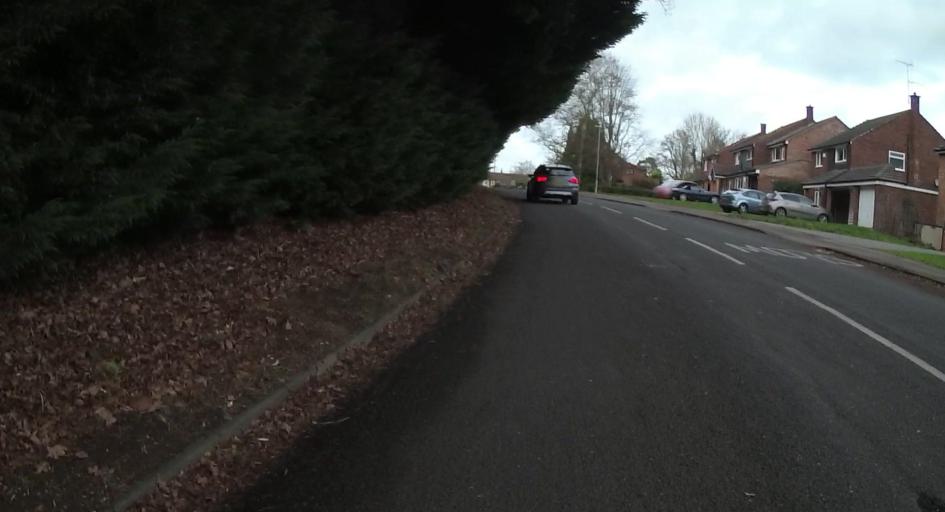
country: GB
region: England
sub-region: Wokingham
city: Wokingham
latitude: 51.4040
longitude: -0.8531
